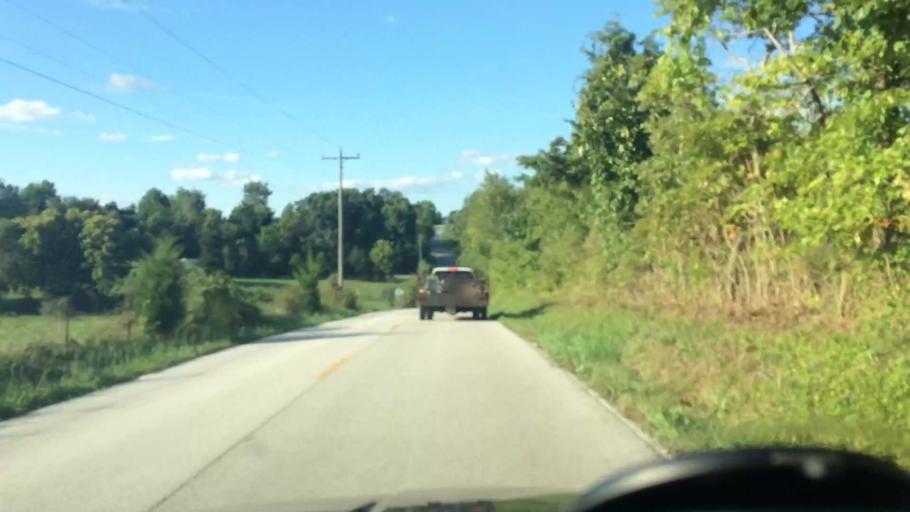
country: US
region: Missouri
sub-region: Greene County
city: Strafford
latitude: 37.2847
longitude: -93.0923
